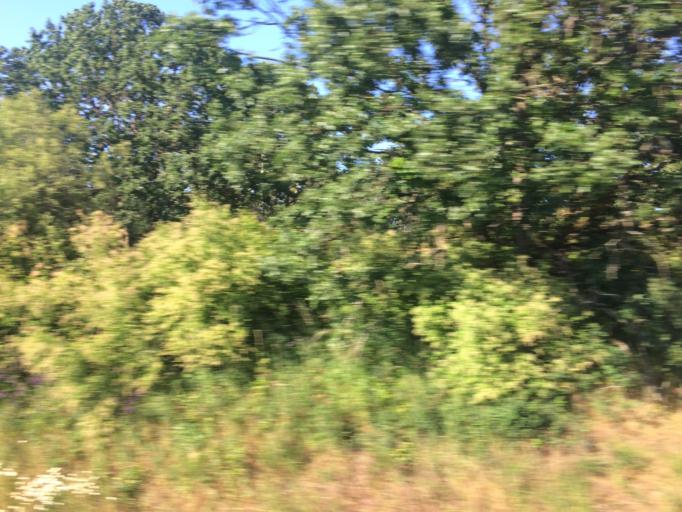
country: CA
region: British Columbia
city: Victoria
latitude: 48.4616
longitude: -123.4108
